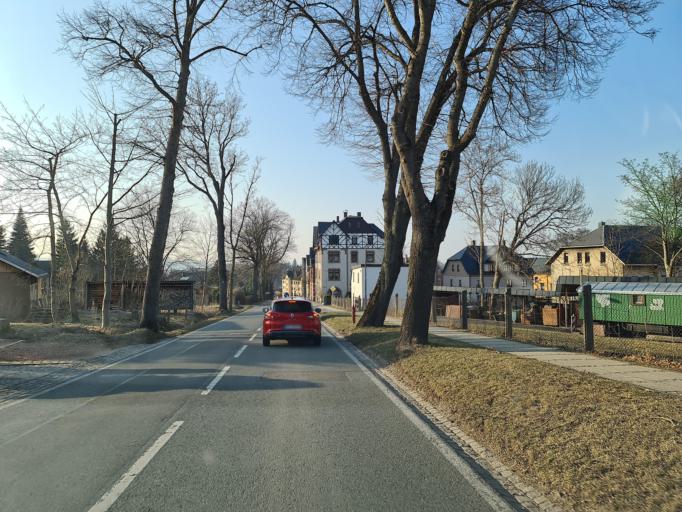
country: DE
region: Saxony
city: Eibenstock
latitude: 50.4909
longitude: 12.6061
